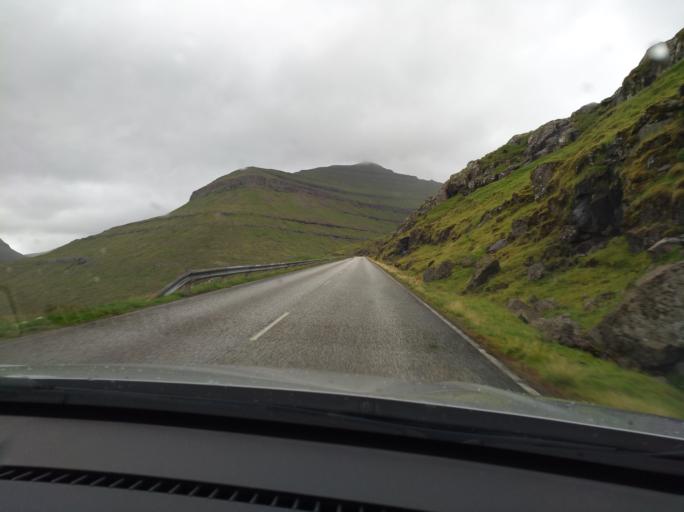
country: FO
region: Eysturoy
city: Fuglafjordur
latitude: 62.2191
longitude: -6.8681
